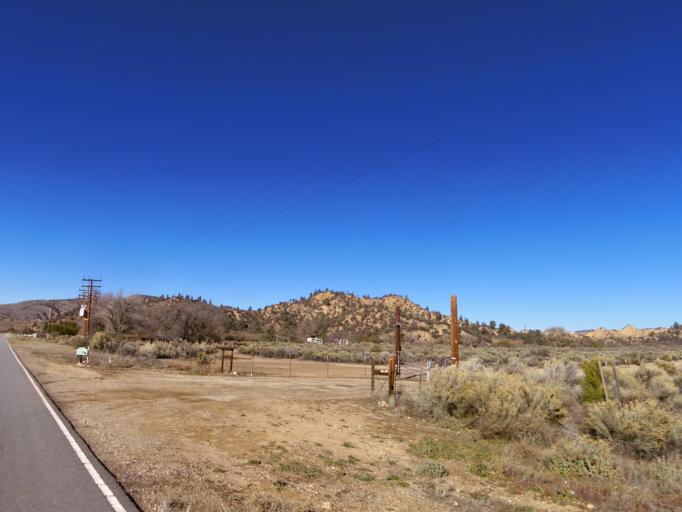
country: US
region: California
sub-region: Kern County
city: Pine Mountain Club
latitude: 34.7108
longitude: -119.3793
